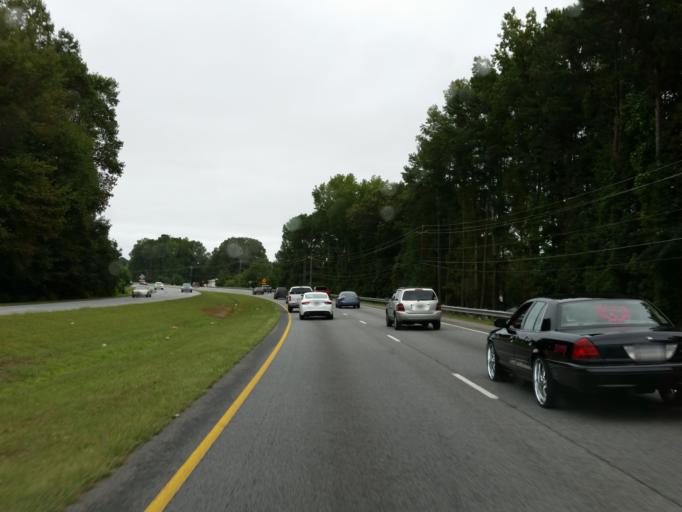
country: US
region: Georgia
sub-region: Clayton County
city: Bonanza
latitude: 33.4666
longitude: -84.3356
